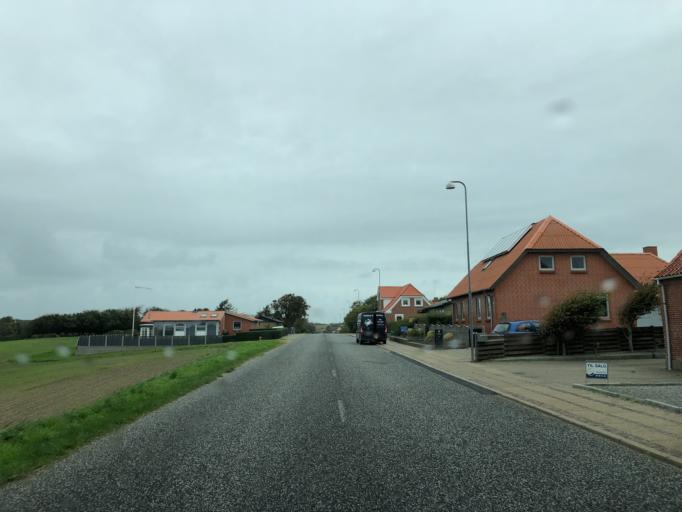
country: DK
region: North Denmark
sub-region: Thisted Kommune
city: Hurup
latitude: 56.7098
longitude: 8.4084
